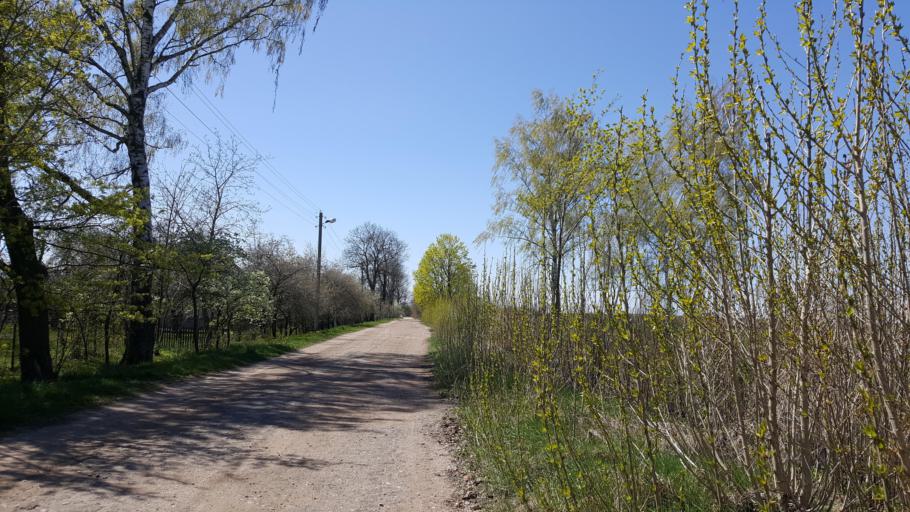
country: BY
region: Brest
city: Charnawchytsy
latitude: 52.3261
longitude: 23.6345
